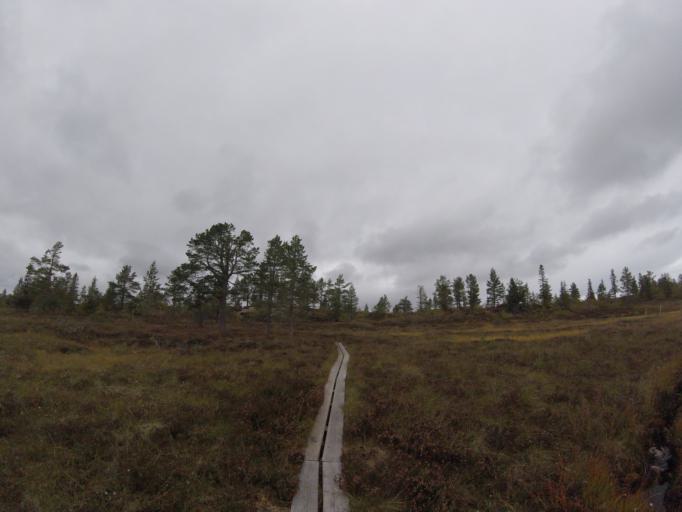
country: NO
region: Buskerud
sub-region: Flesberg
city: Lampeland
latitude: 59.7572
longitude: 9.4033
